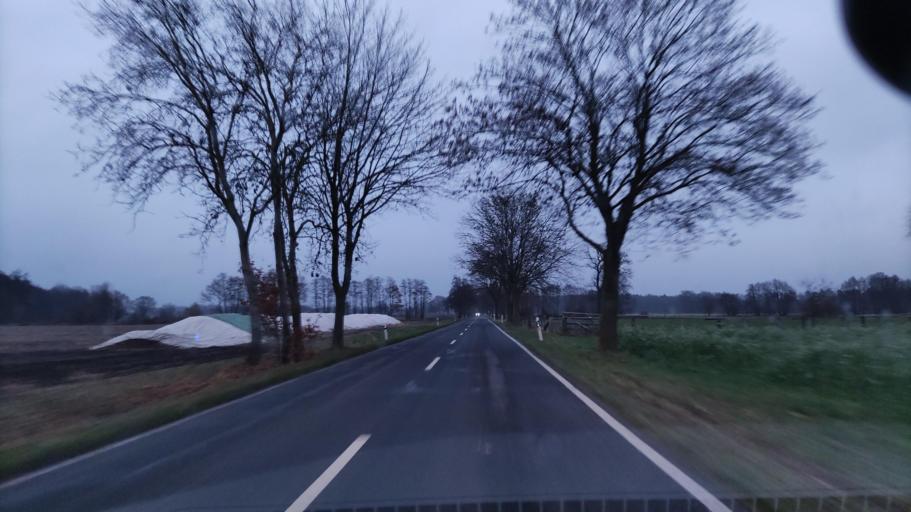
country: DE
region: Lower Saxony
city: Waddeweitz
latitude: 53.0265
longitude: 11.0156
